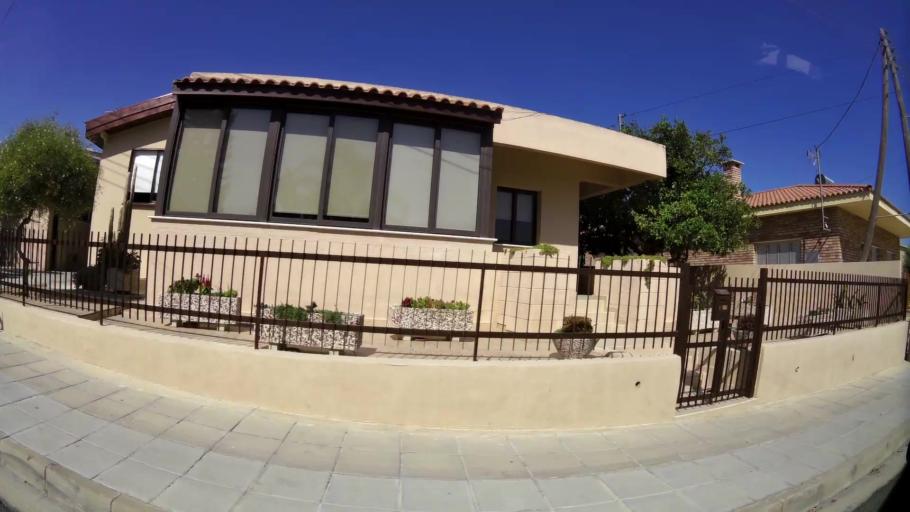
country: CY
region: Larnaka
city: Livadia
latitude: 34.9494
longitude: 33.6196
